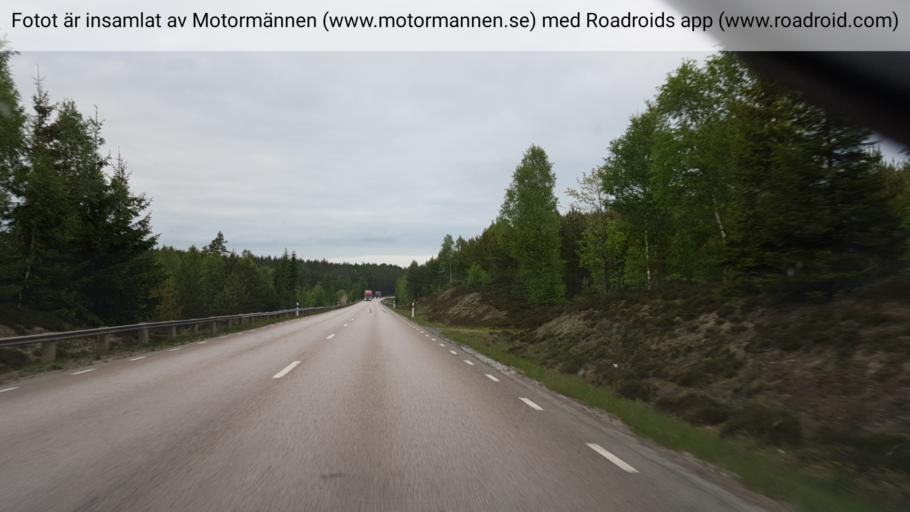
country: SE
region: Joenkoeping
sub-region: Mullsjo Kommun
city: Mullsjoe
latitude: 58.0445
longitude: 13.8486
